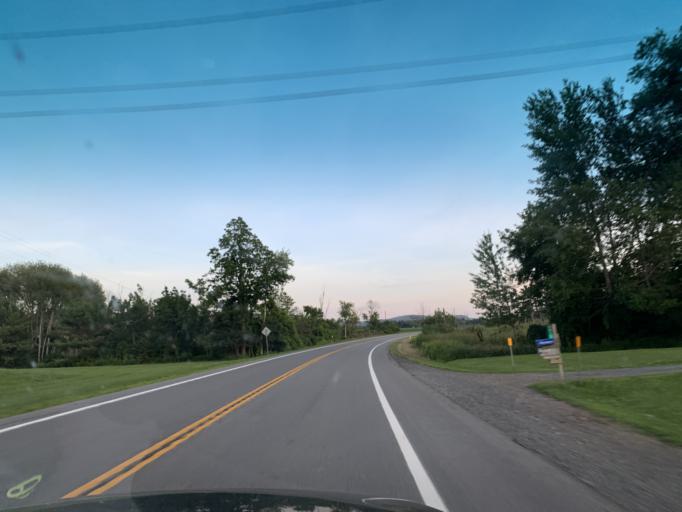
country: US
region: New York
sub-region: Oneida County
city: Chadwicks
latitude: 42.9131
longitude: -75.2404
